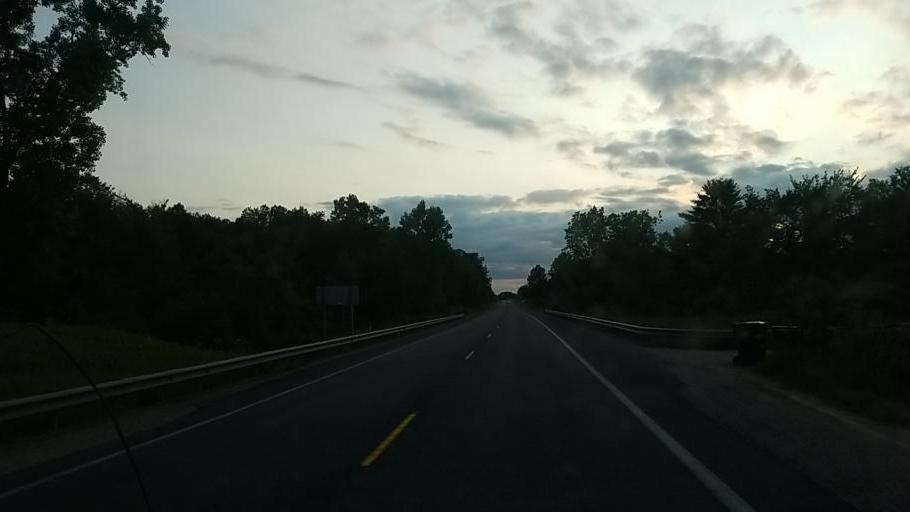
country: US
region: Michigan
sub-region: Newaygo County
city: Newaygo
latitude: 43.4055
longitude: -85.7742
